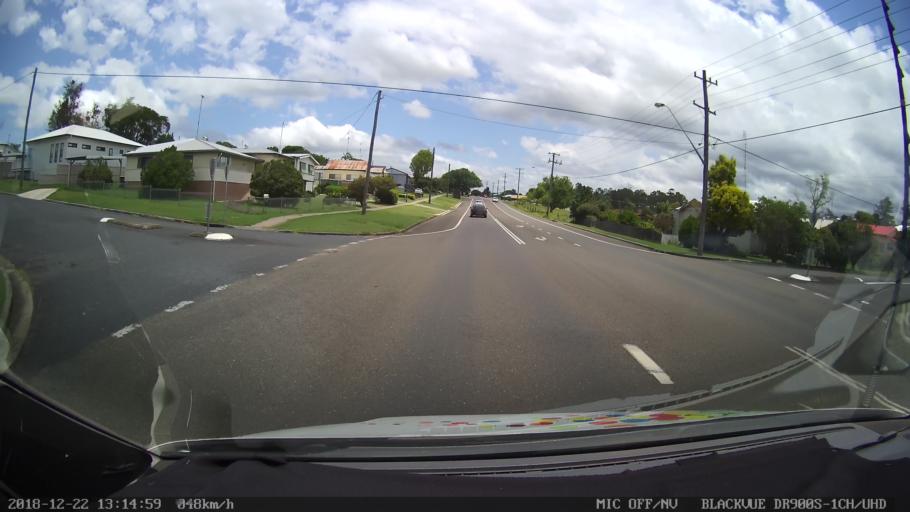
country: AU
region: New South Wales
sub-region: Clarence Valley
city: South Grafton
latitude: -29.7144
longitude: 152.9400
